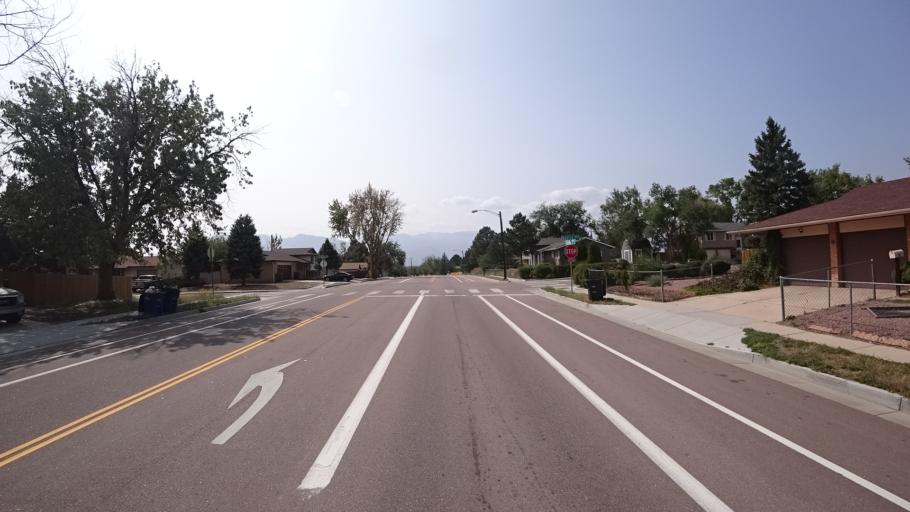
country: US
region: Colorado
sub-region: El Paso County
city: Stratmoor
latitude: 38.8056
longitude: -104.7689
